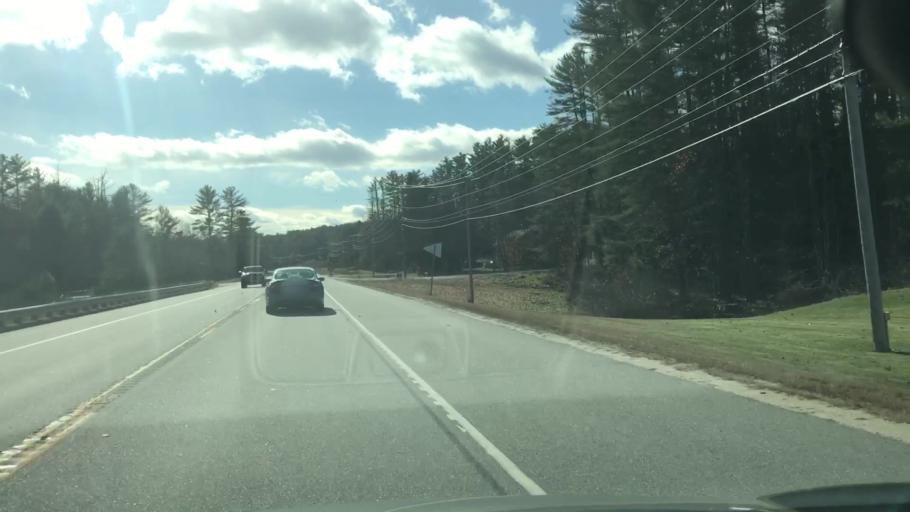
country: US
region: New Hampshire
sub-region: Belknap County
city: Barnstead
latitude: 43.3302
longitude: -71.3025
